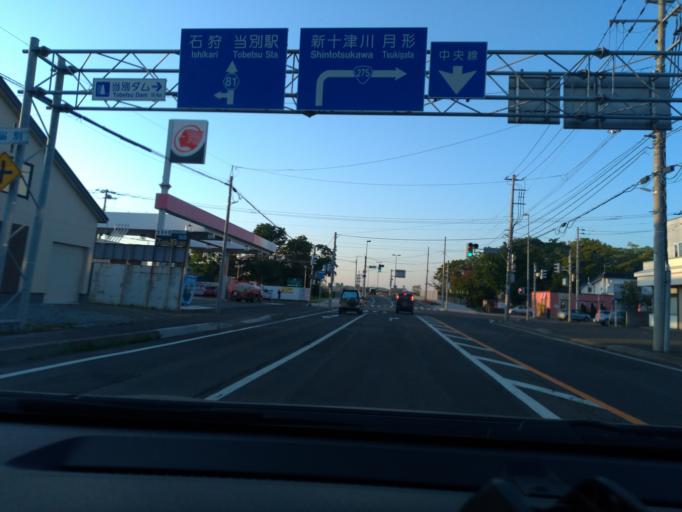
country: JP
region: Hokkaido
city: Tobetsu
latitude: 43.2115
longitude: 141.5182
